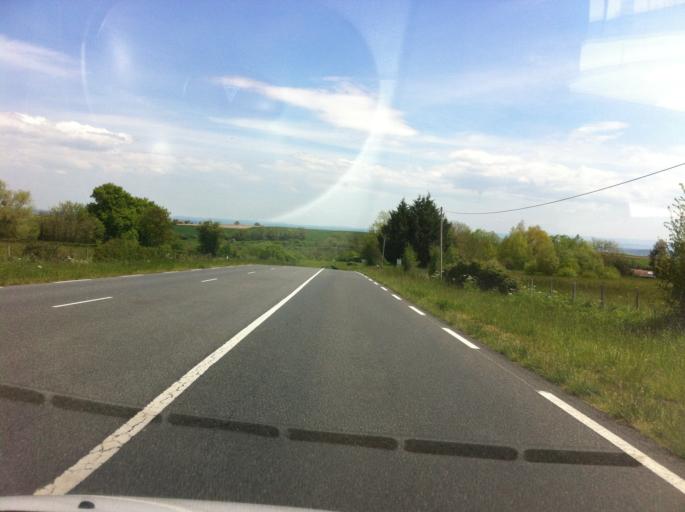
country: FR
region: Auvergne
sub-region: Departement de l'Allier
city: Saint-Pourcain-sur-Sioule
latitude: 46.3138
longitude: 3.2151
